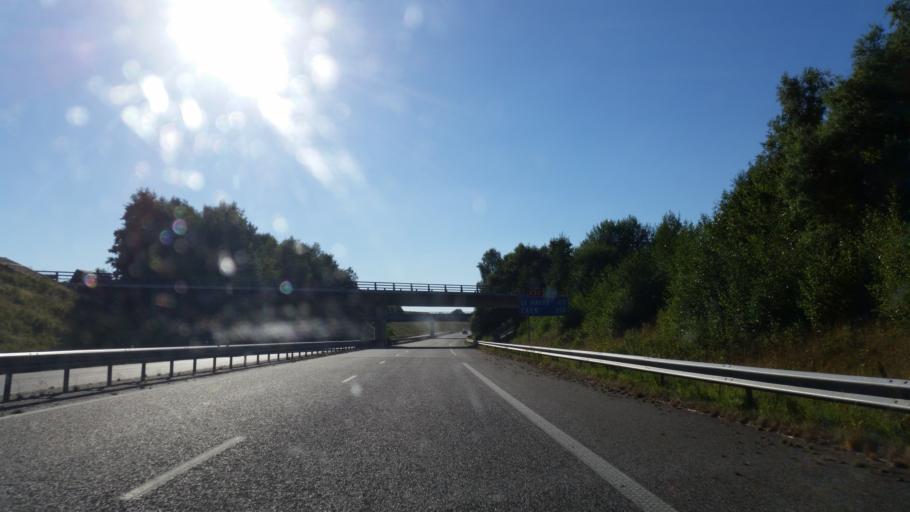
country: FR
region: Haute-Normandie
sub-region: Departement de la Seine-Maritime
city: Yerville
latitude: 49.6529
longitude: 0.8365
